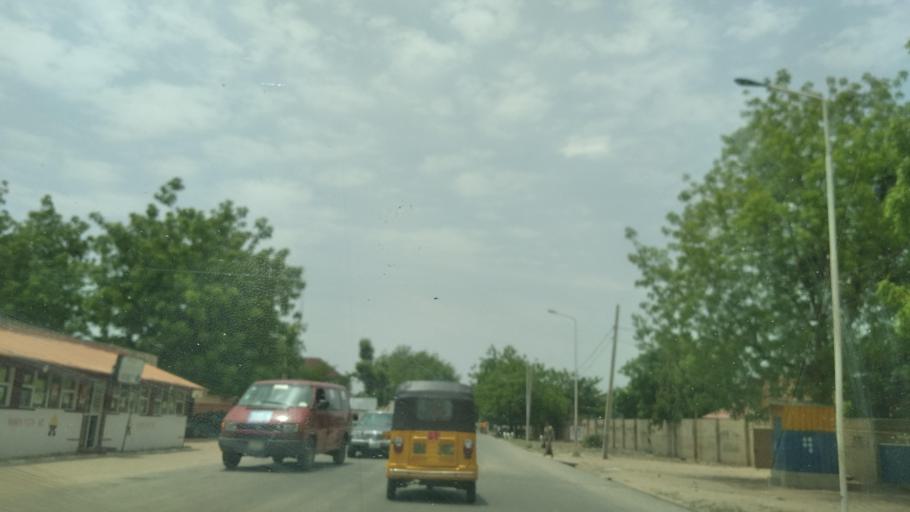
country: NG
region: Borno
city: Maiduguri
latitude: 11.8071
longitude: 13.1578
